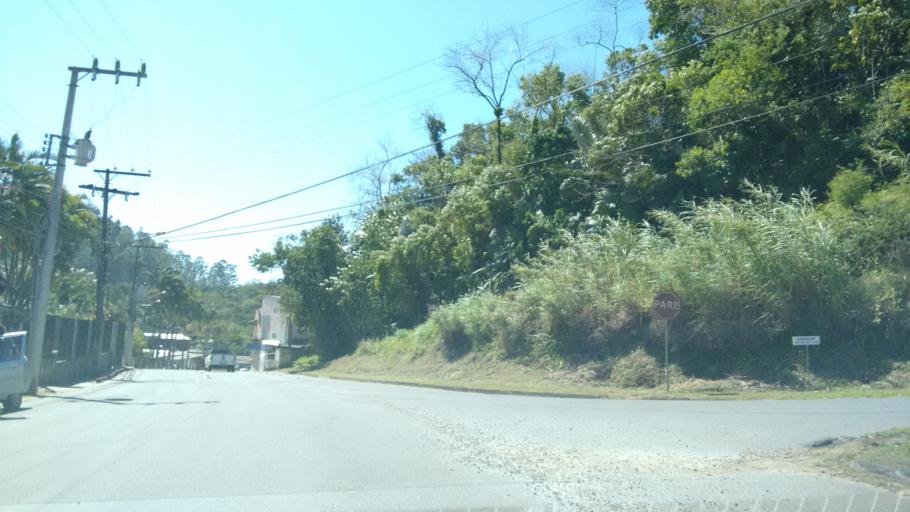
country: BR
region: Santa Catarina
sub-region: Blumenau
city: Blumenau
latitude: -26.8805
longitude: -49.1219
